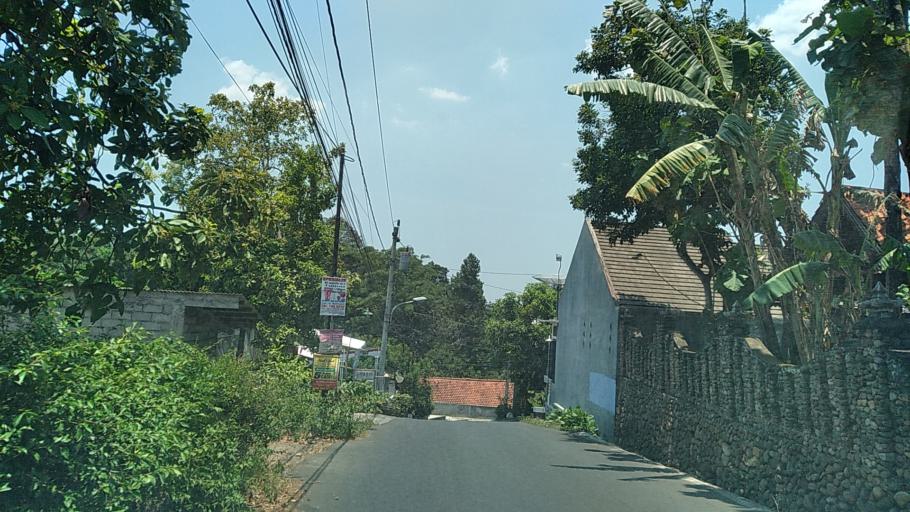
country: ID
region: Central Java
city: Ungaran
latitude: -7.0795
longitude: 110.4228
